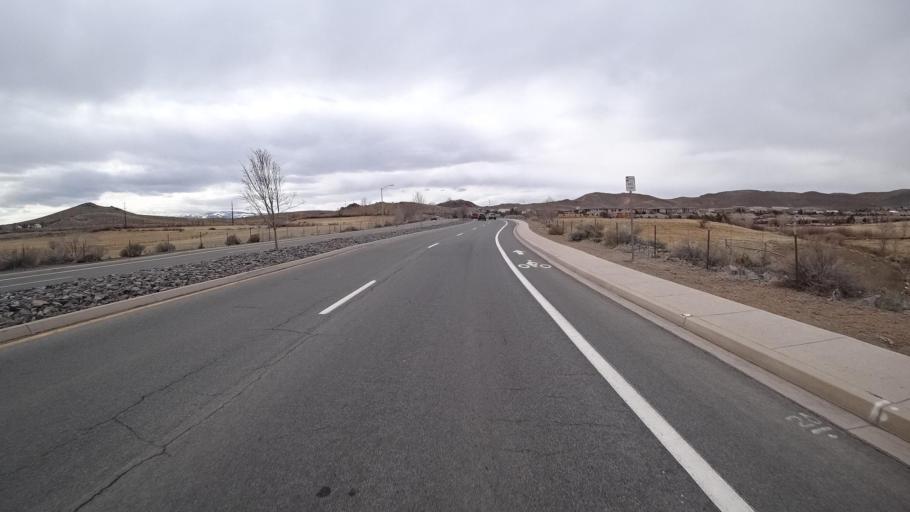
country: US
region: Nevada
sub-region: Washoe County
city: Sparks
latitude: 39.5756
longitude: -119.7305
